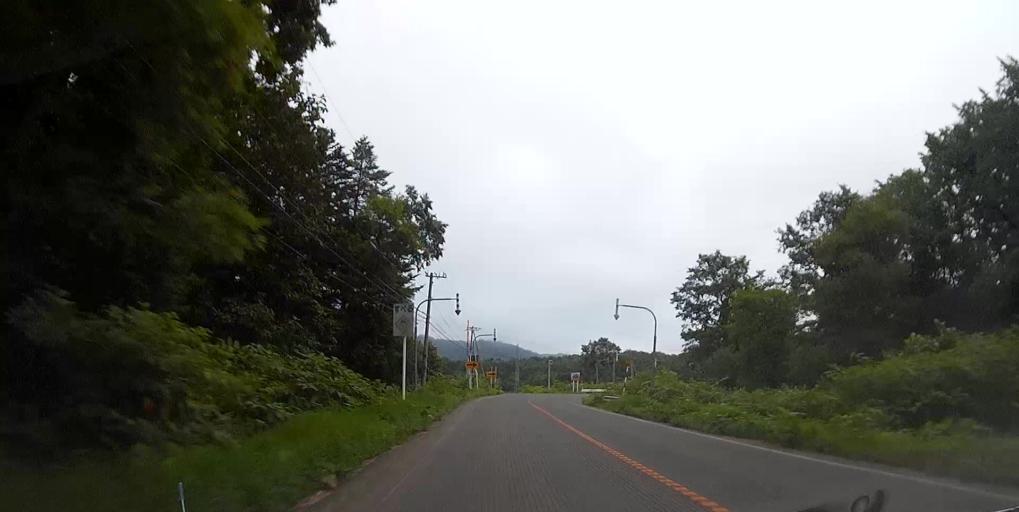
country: JP
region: Hokkaido
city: Nanae
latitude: 42.2948
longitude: 140.1396
